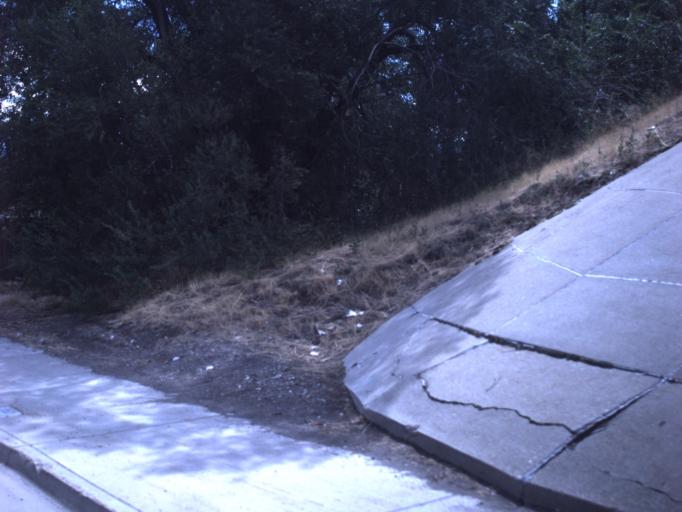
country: US
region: Utah
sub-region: Salt Lake County
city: Taylorsville
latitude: 40.6529
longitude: -111.9522
